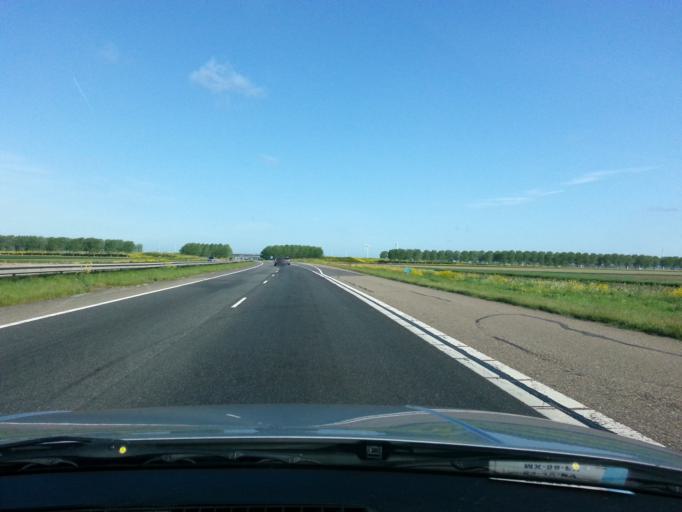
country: NL
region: Utrecht
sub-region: Gemeente Bunschoten
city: Spakenburg
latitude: 52.3439
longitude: 5.3425
